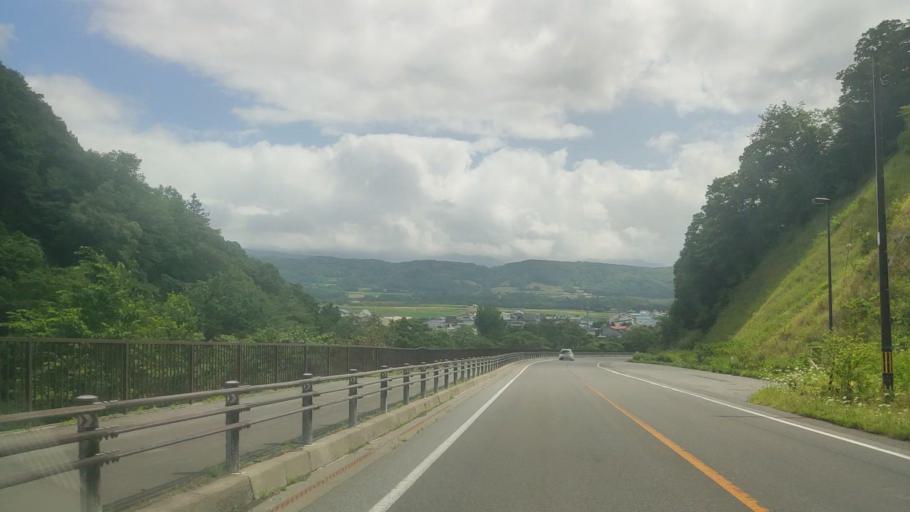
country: JP
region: Hokkaido
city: Date
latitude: 42.5616
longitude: 140.8855
